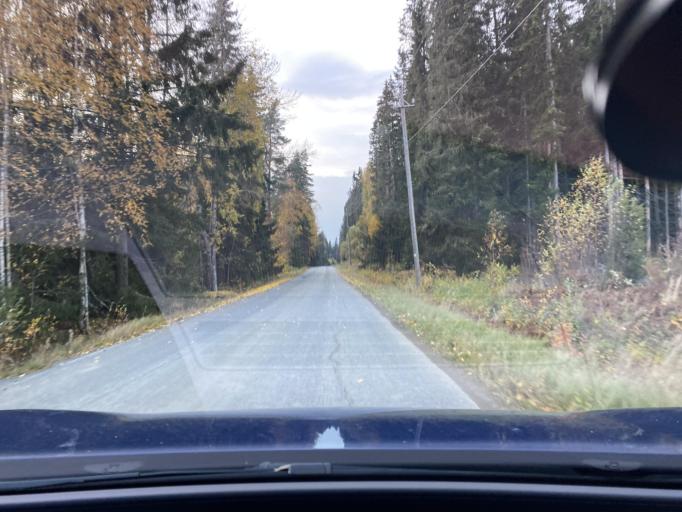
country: FI
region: Varsinais-Suomi
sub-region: Loimaa
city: Alastaro
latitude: 61.0804
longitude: 22.9501
